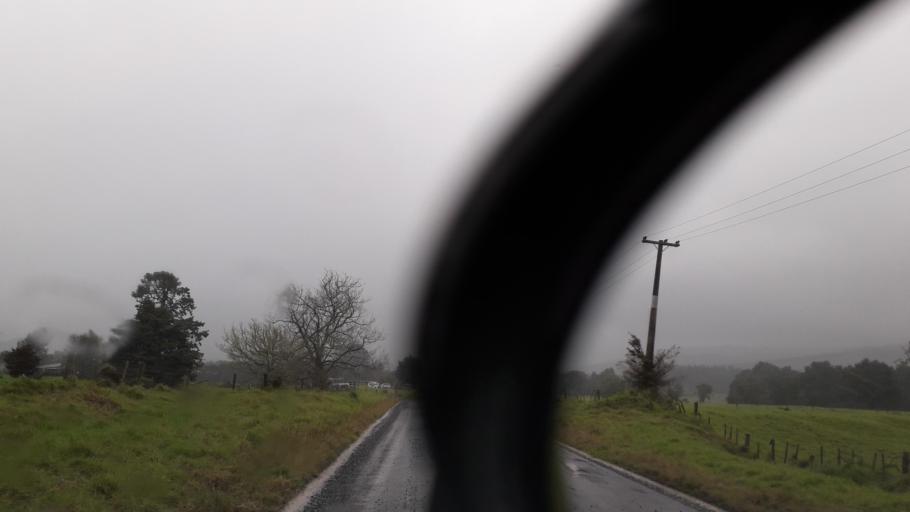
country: NZ
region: Northland
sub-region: Far North District
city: Waimate North
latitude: -35.4999
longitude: 173.6988
